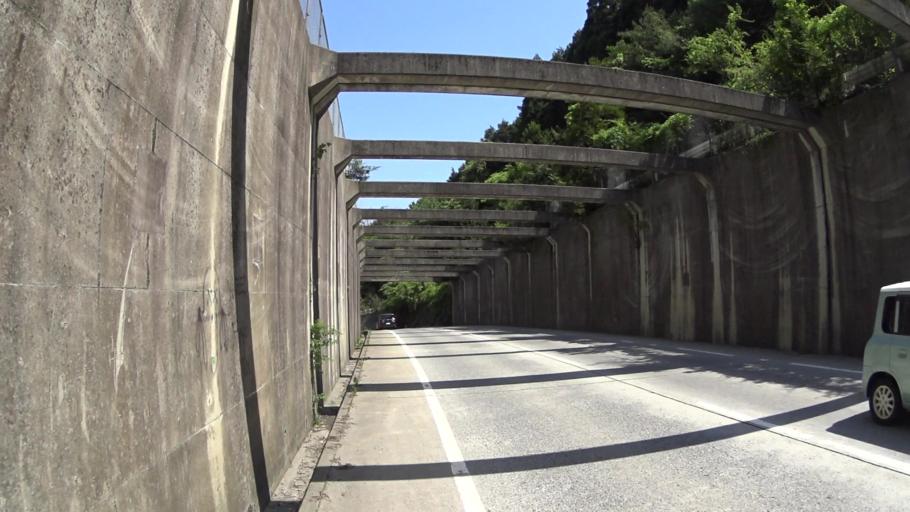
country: JP
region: Shiga Prefecture
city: Kitahama
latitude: 35.1600
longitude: 135.8525
